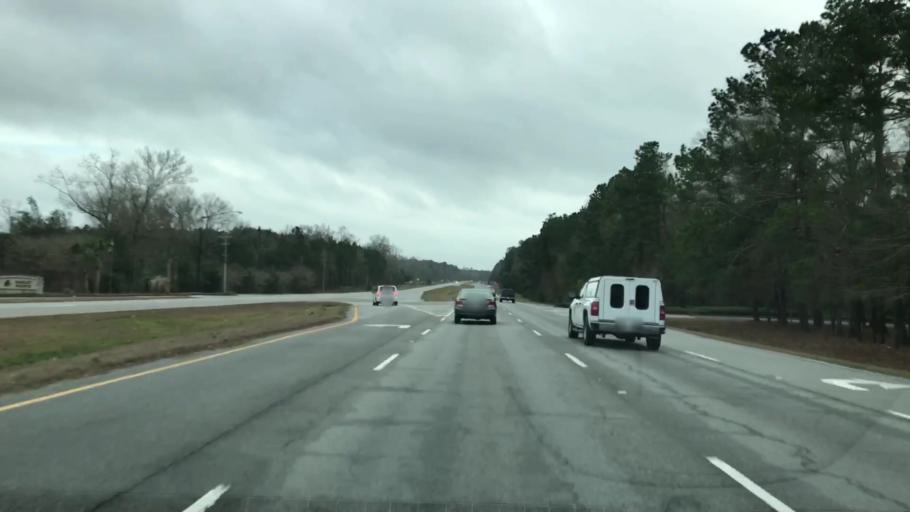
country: US
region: South Carolina
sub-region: Berkeley County
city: Moncks Corner
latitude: 33.1324
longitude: -80.0310
